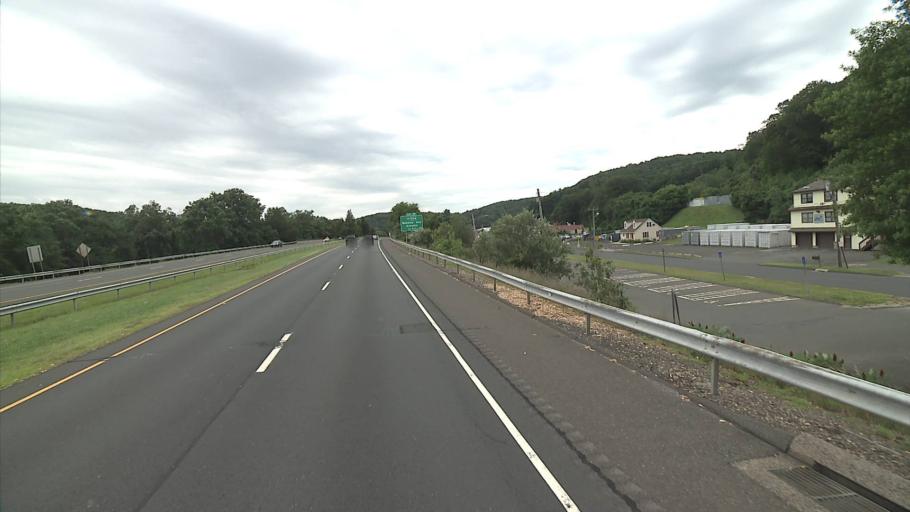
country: US
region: Connecticut
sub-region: New Haven County
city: Ansonia
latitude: 41.3702
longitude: -73.0862
